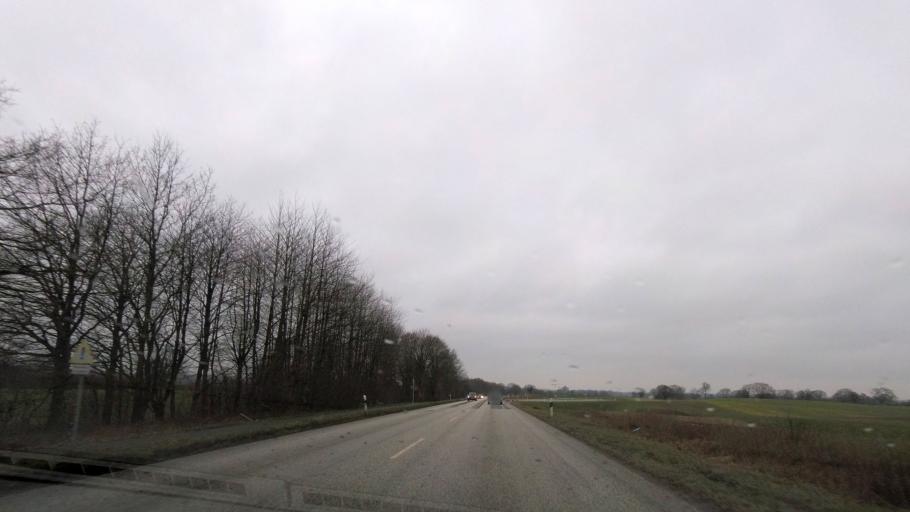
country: DE
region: Schleswig-Holstein
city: Warnau
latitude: 54.1943
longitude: 10.1596
